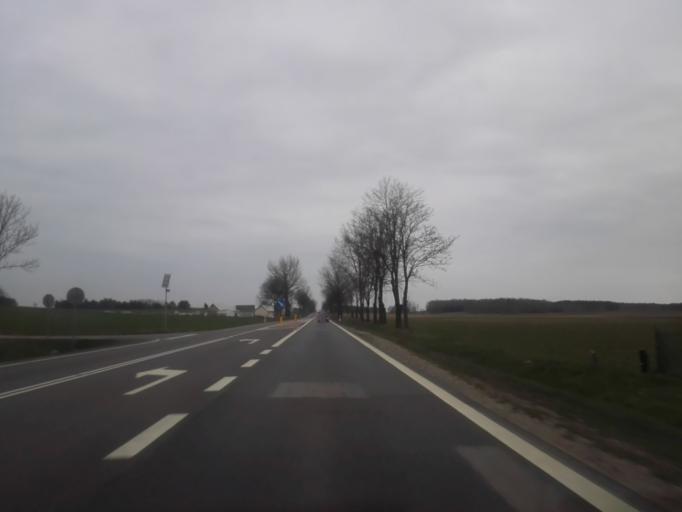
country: PL
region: Podlasie
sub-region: Powiat kolnenski
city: Stawiski
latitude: 53.4604
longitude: 22.1958
